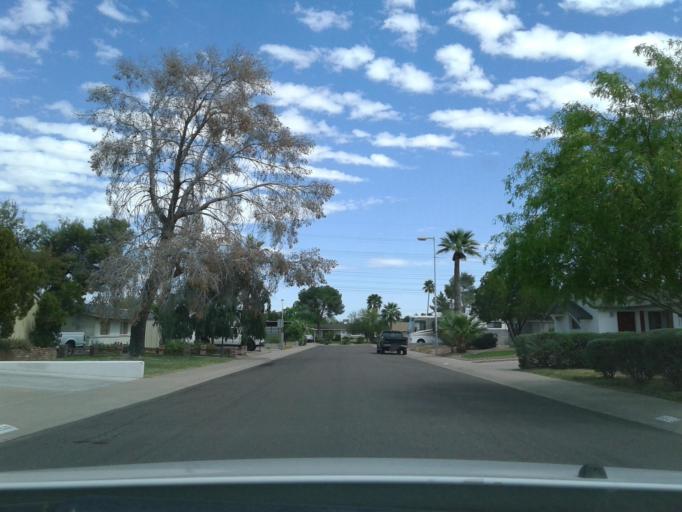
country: US
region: Arizona
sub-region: Maricopa County
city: Tempe Junction
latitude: 33.4707
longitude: -111.9405
